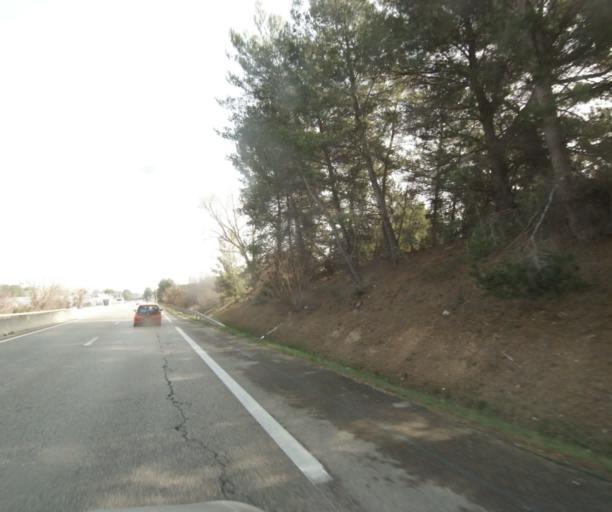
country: FR
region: Provence-Alpes-Cote d'Azur
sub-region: Departement des Bouches-du-Rhone
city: Simiane-Collongue
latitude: 43.4467
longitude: 5.4423
